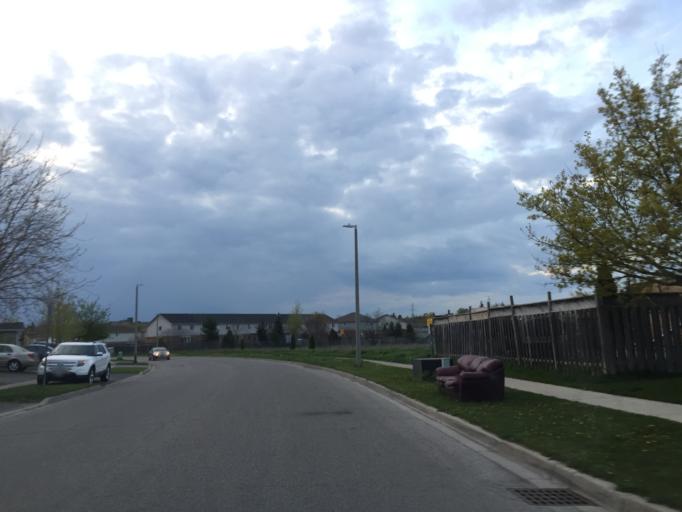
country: CA
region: Ontario
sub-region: Wellington County
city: Guelph
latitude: 43.5278
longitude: -80.2752
